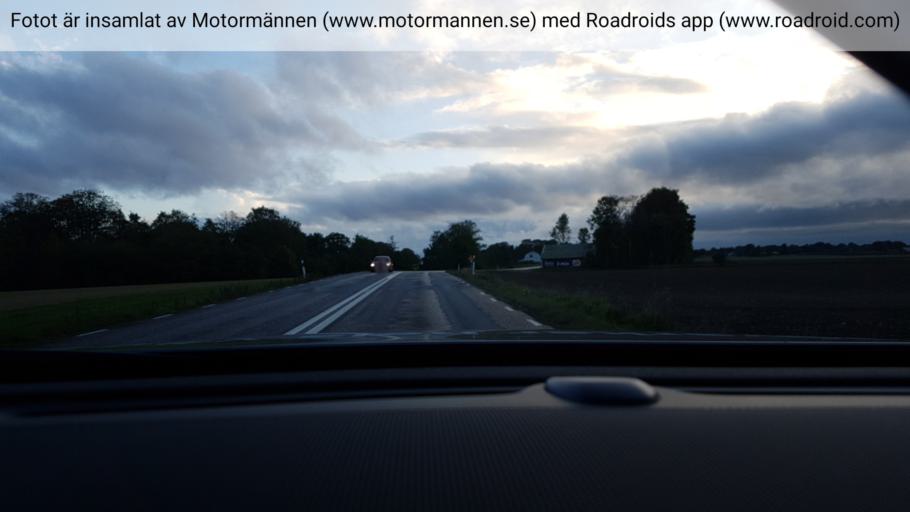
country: SE
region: Vaestra Goetaland
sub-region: Vanersborgs Kommun
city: Bralanda
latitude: 58.5710
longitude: 12.3816
